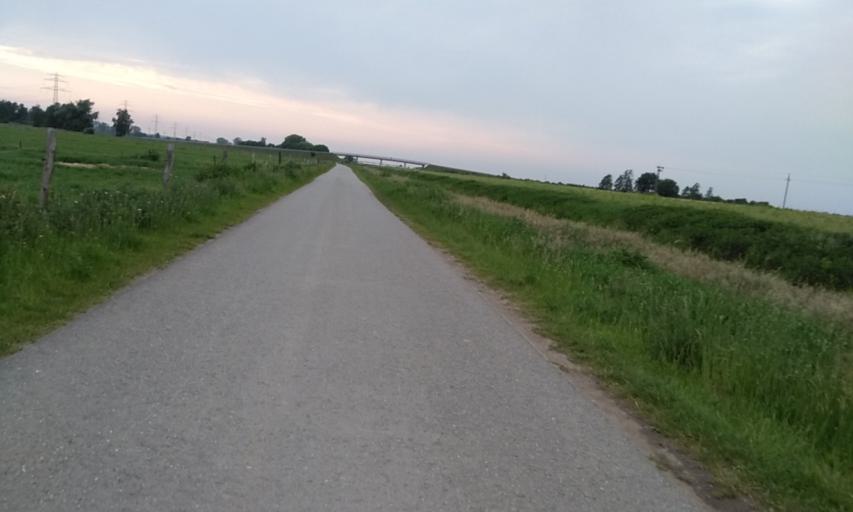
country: DE
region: Lower Saxony
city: Buxtehude
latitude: 53.4937
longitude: 9.6866
